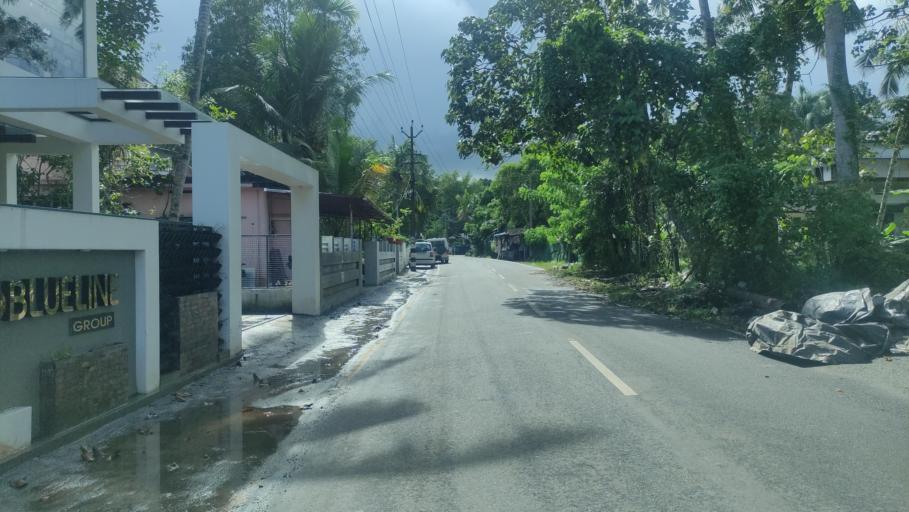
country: IN
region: Kerala
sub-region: Alappuzha
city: Kayankulam
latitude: 9.1952
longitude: 76.5076
